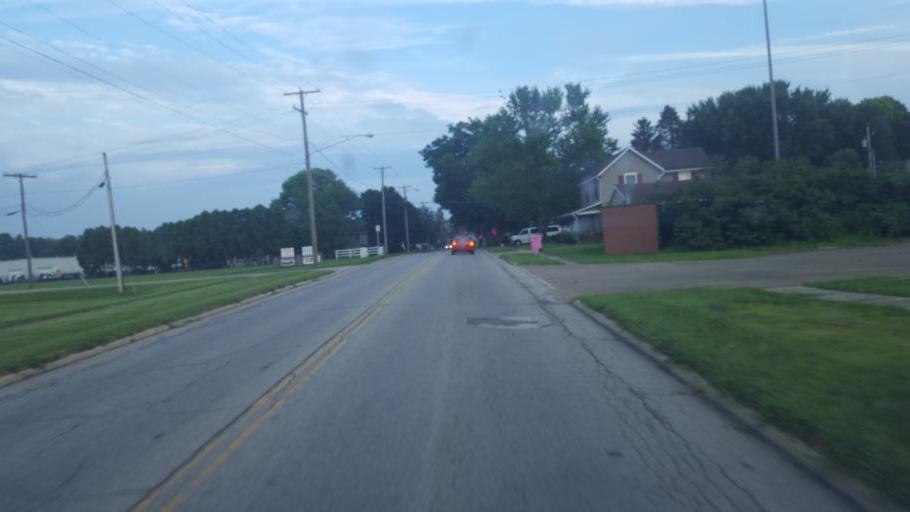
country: US
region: Ohio
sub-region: Richland County
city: Lexington
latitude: 40.6829
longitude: -82.5839
